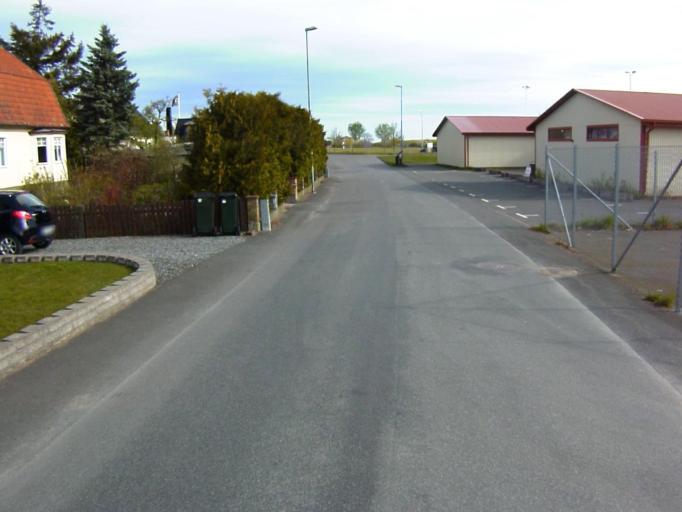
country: SE
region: Skane
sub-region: Kristianstads Kommun
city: Kristianstad
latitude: 56.0198
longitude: 14.1232
